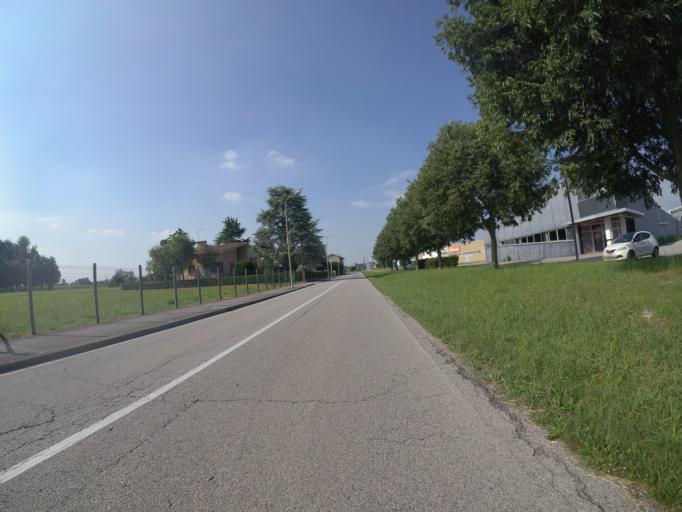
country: IT
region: Friuli Venezia Giulia
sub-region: Provincia di Udine
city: Codroipo
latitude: 45.9489
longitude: 12.9721
